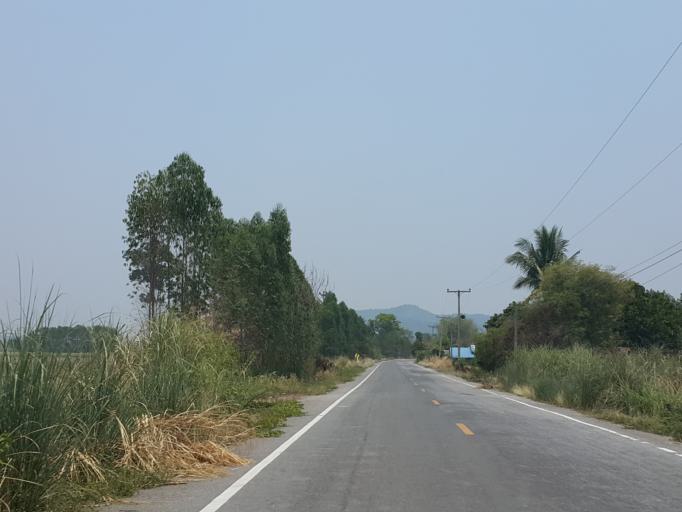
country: TH
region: Kamphaeng Phet
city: Pang Sila Thong
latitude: 16.0553
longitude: 99.3615
